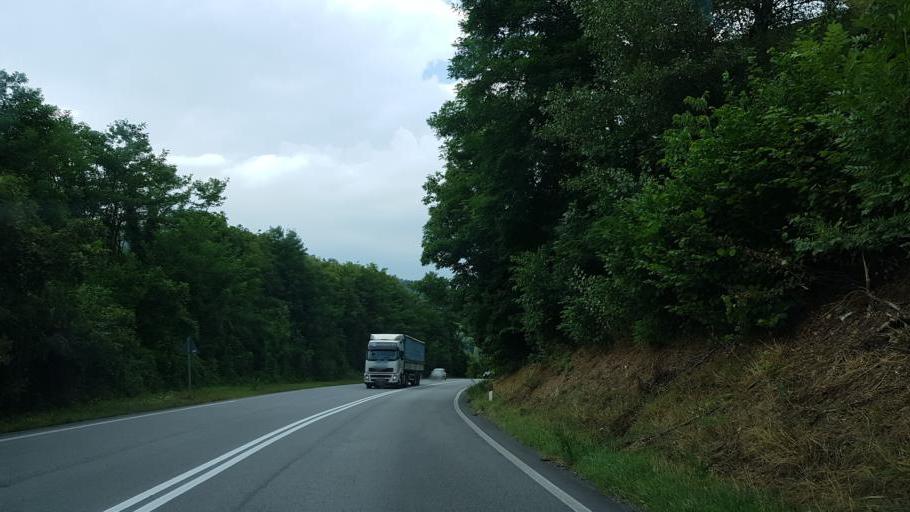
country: IT
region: Piedmont
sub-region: Provincia di Cuneo
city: Borgo San Dalmazzo
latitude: 44.3396
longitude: 7.4765
